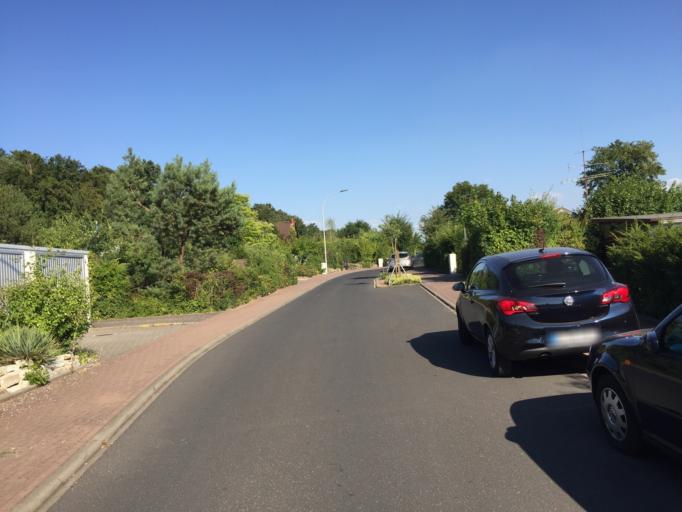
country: DE
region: Hesse
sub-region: Regierungsbezirk Giessen
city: Hoernsheim
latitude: 50.5426
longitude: 8.6618
